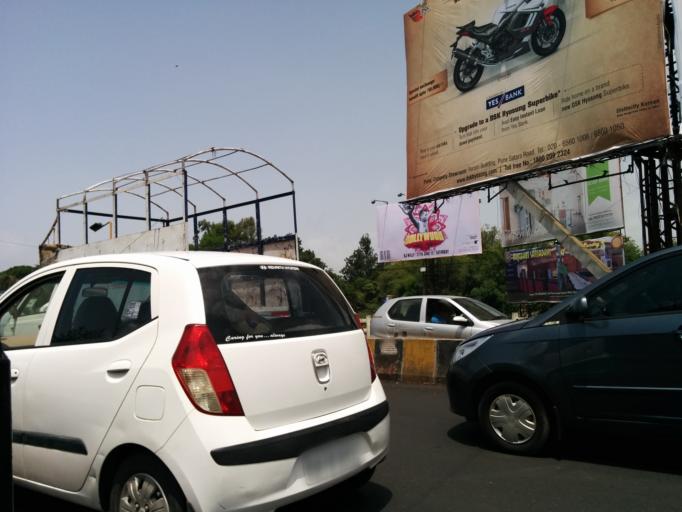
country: IN
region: Maharashtra
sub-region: Pune Division
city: Shivaji Nagar
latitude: 18.5395
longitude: 73.9038
